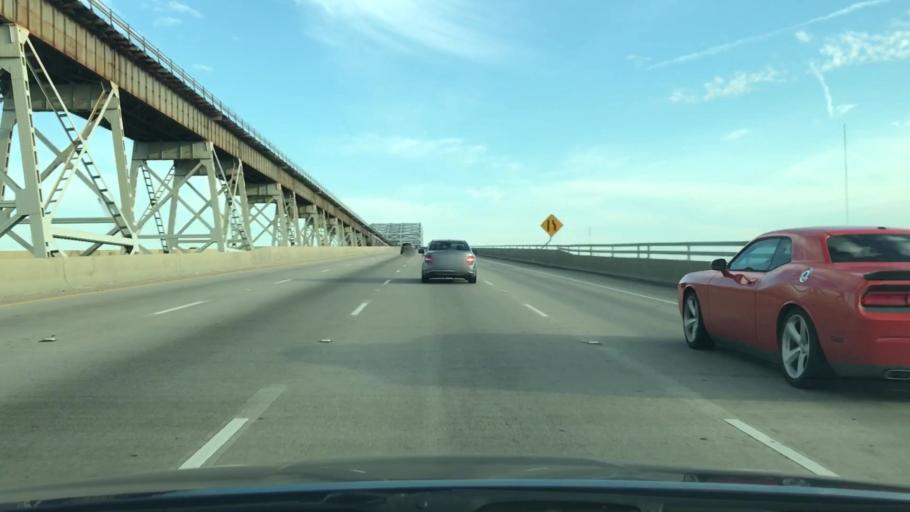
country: US
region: Louisiana
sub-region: Jefferson Parish
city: Elmwood
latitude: 29.9501
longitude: -90.1759
